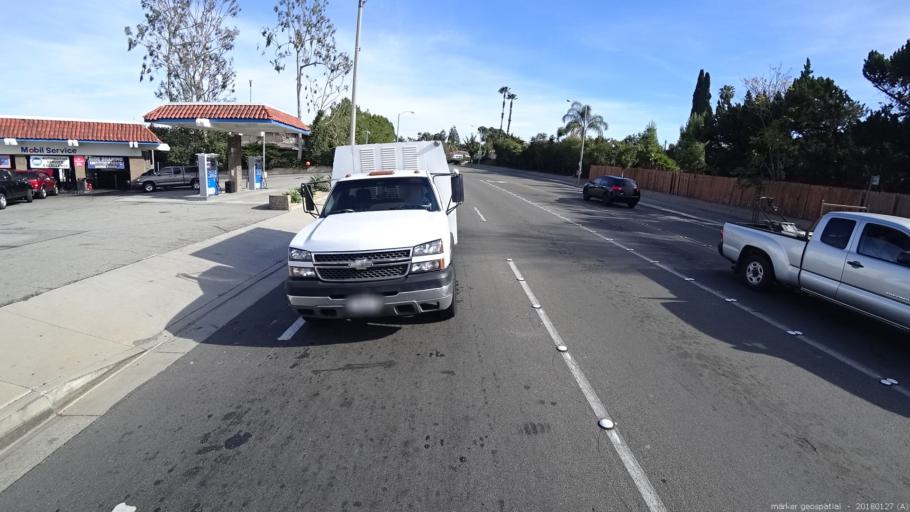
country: US
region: California
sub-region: Los Angeles County
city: Diamond Bar
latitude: 34.0192
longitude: -117.8083
